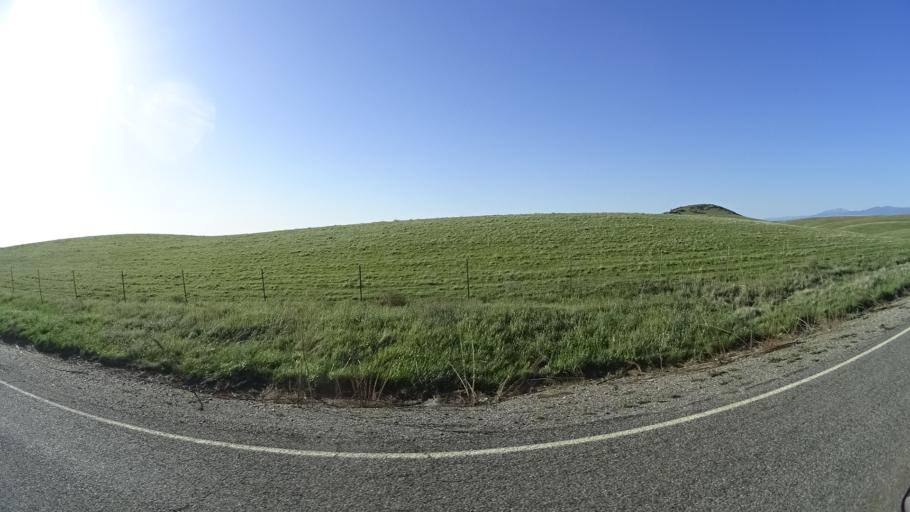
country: US
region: California
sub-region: Glenn County
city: Orland
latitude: 39.8309
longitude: -122.3474
